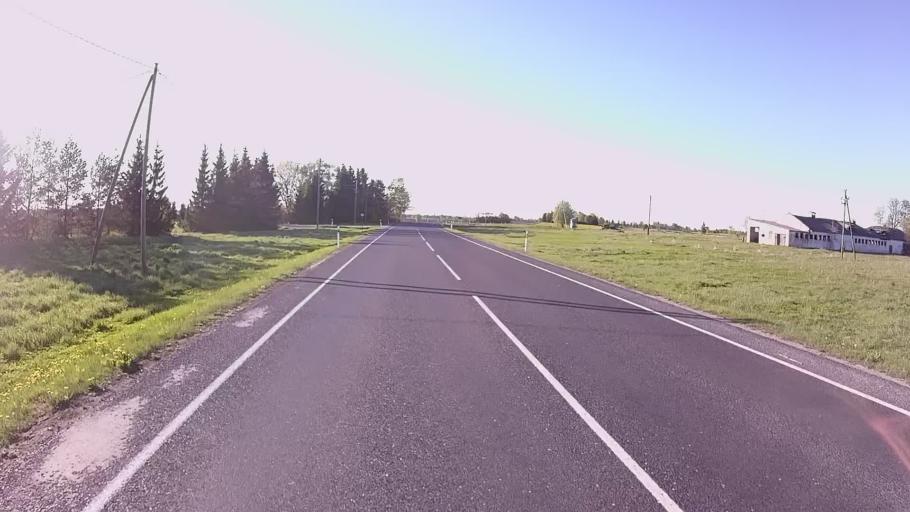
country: EE
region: Viljandimaa
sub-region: Vohma linn
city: Vohma
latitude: 58.6603
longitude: 25.6090
